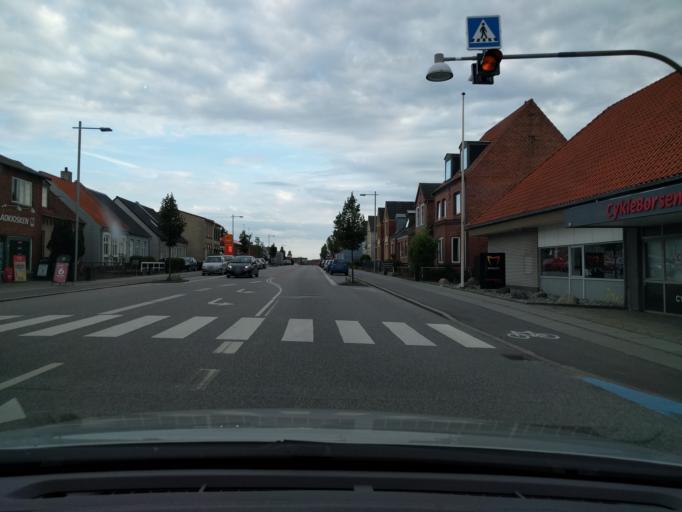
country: DK
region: Zealand
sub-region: Guldborgsund Kommune
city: Nykobing Falster
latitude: 54.7785
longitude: 11.8669
